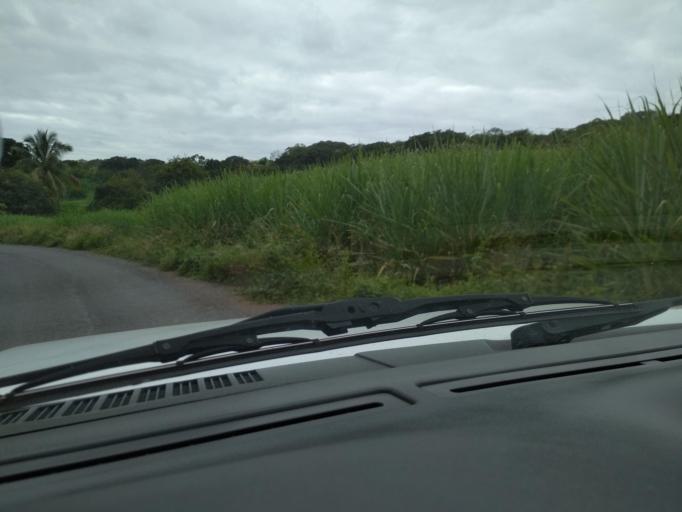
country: MX
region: Veracruz
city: Alto Lucero
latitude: 19.5889
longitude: -96.7893
